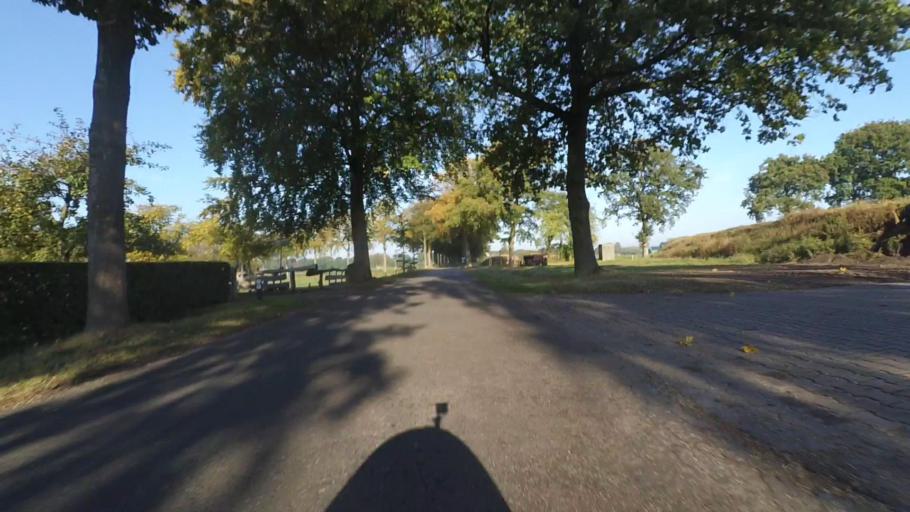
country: NL
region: Gelderland
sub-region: Gemeente Epe
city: Vaassen
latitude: 52.2944
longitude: 5.9538
